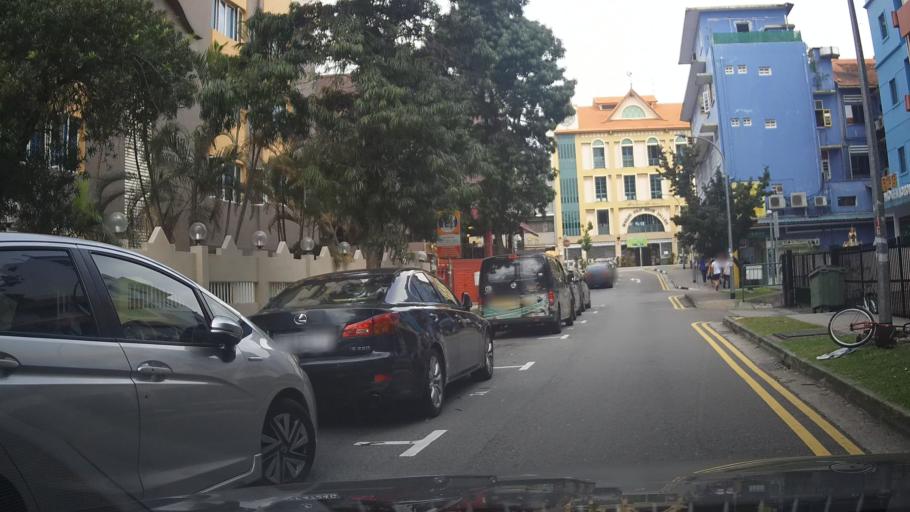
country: SG
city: Singapore
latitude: 1.3119
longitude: 103.8779
